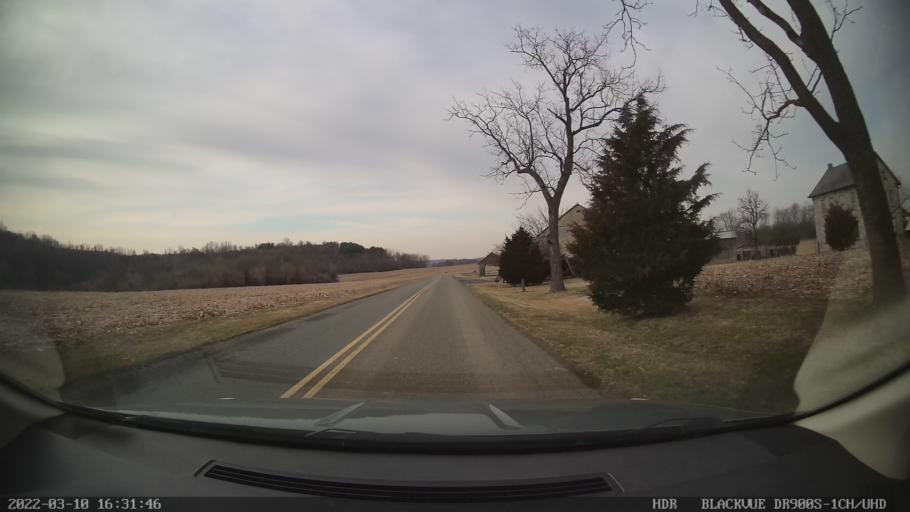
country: US
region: Pennsylvania
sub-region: Berks County
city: Oley
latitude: 40.3562
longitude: -75.7877
